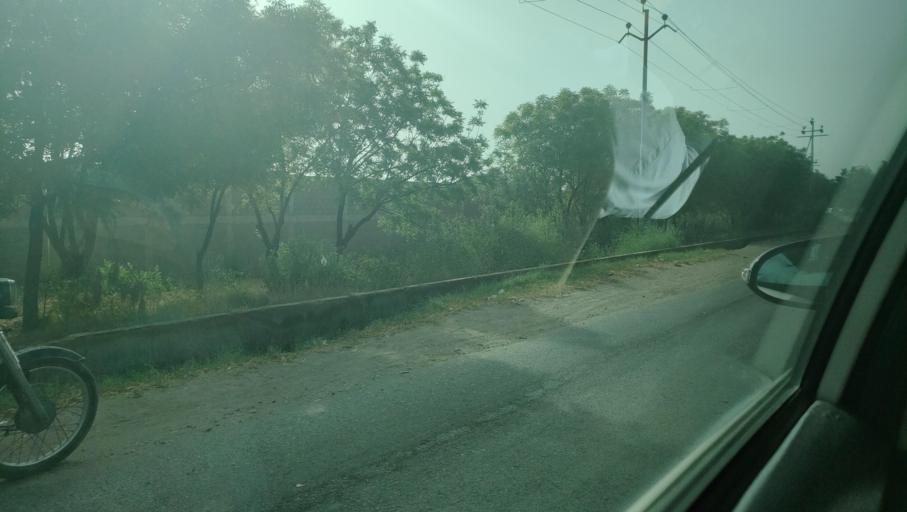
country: PK
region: Sindh
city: Malir Cantonment
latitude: 24.9254
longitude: 67.1803
